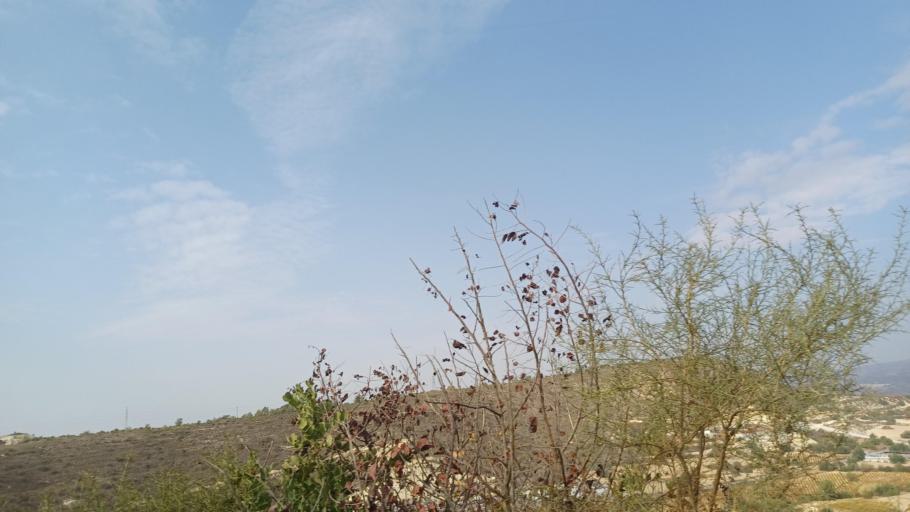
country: CY
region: Limassol
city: Ypsonas
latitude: 34.7440
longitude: 32.9481
